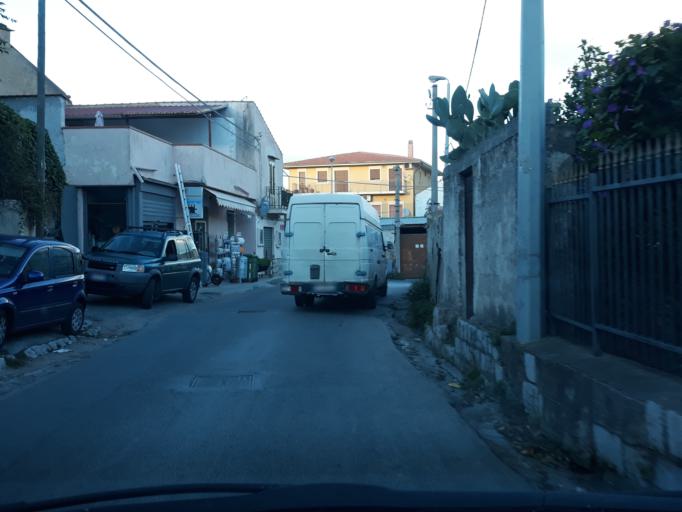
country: IT
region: Sicily
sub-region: Palermo
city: Villa Ciambra
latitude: 38.0783
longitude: 13.3128
